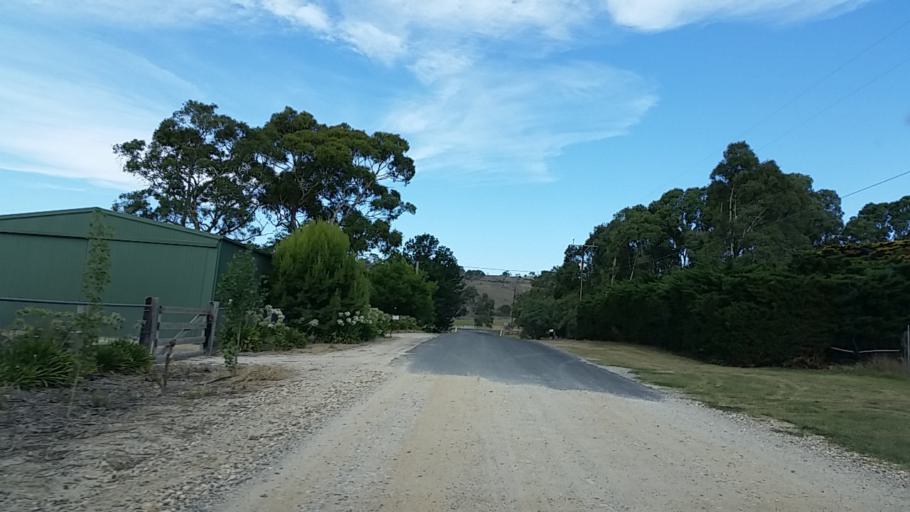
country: AU
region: South Australia
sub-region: Barossa
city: Angaston
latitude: -34.5649
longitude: 139.0859
